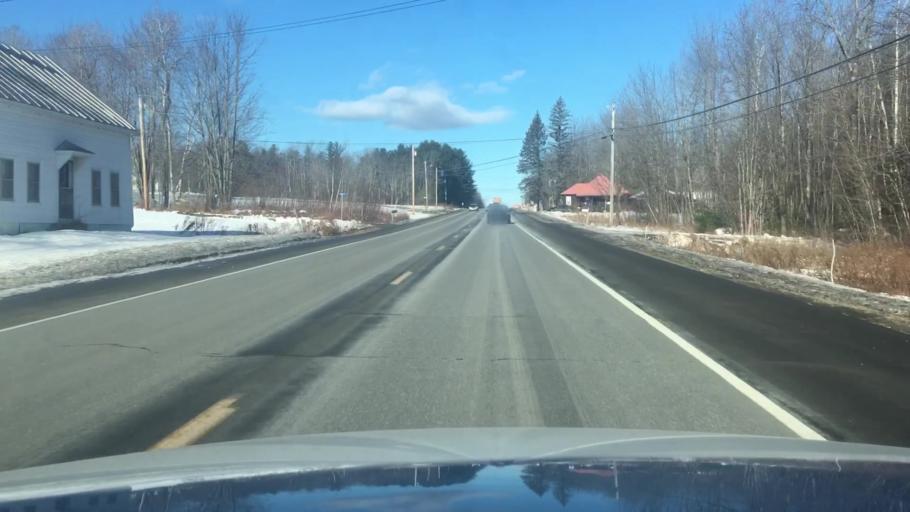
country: US
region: Maine
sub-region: Kennebec County
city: Waterville
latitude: 44.6181
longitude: -69.6700
